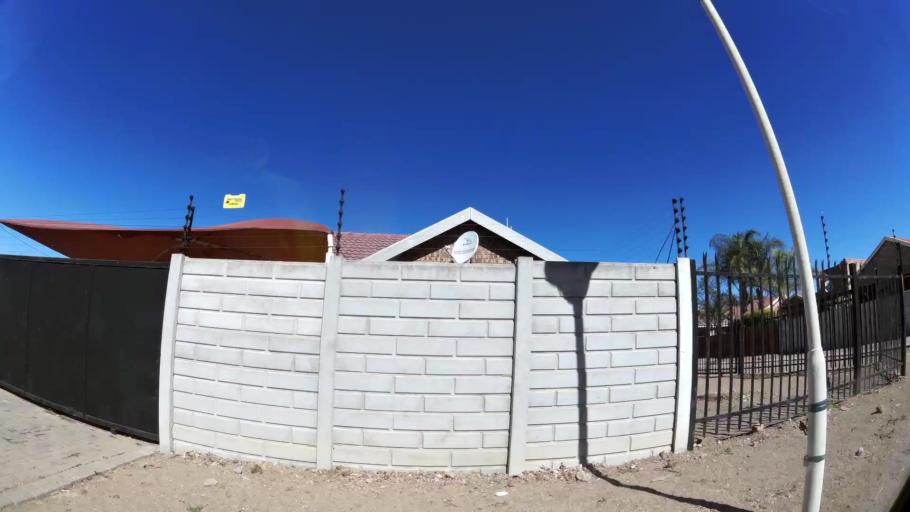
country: ZA
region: Limpopo
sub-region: Capricorn District Municipality
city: Polokwane
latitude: -23.8675
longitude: 29.4283
